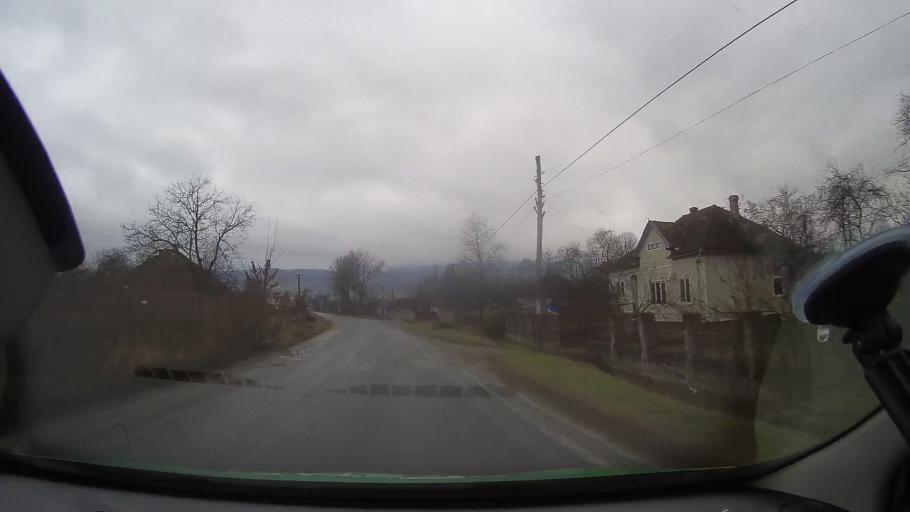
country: RO
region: Arad
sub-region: Comuna Halmagiu
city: Halmagiu
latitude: 46.2597
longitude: 22.5787
